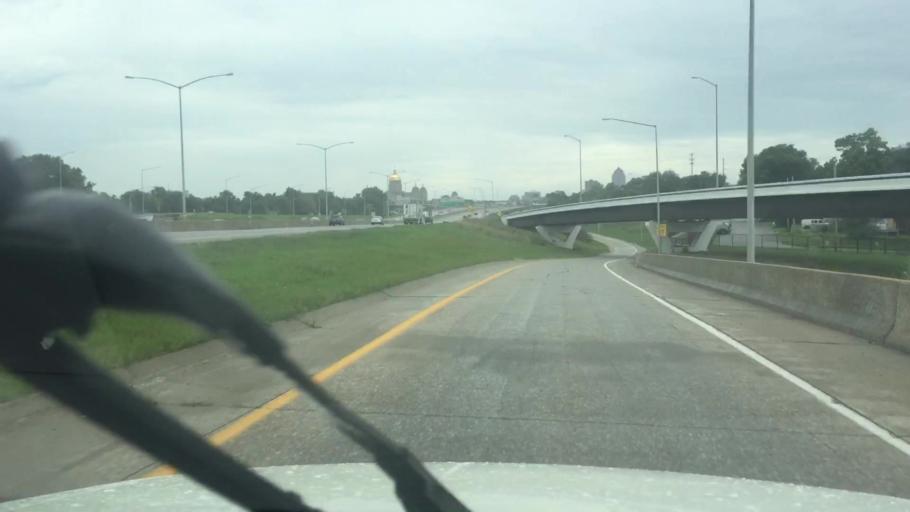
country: US
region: Iowa
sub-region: Polk County
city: Des Moines
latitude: 41.6000
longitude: -93.5875
